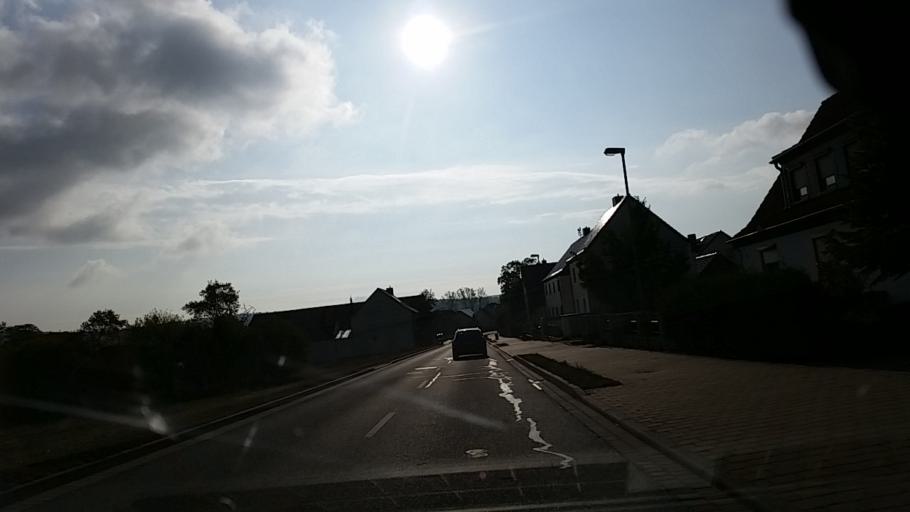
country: DE
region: Thuringia
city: Kleinfurra
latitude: 51.4130
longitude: 10.7616
